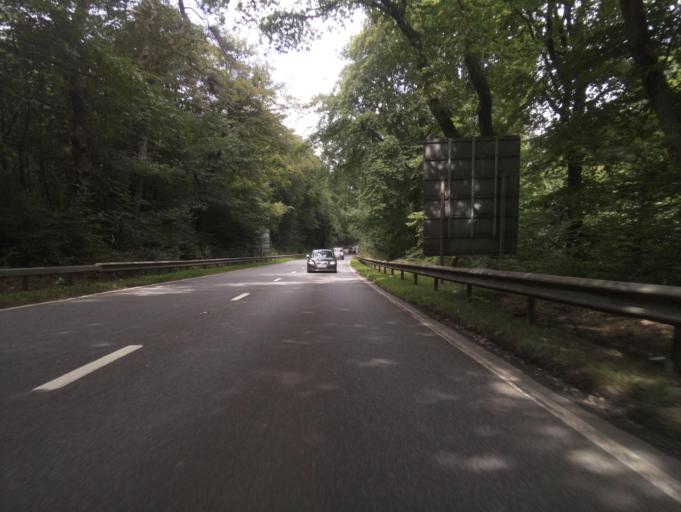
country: GB
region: England
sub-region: Devon
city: Chudleigh
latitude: 50.6125
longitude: -3.5544
